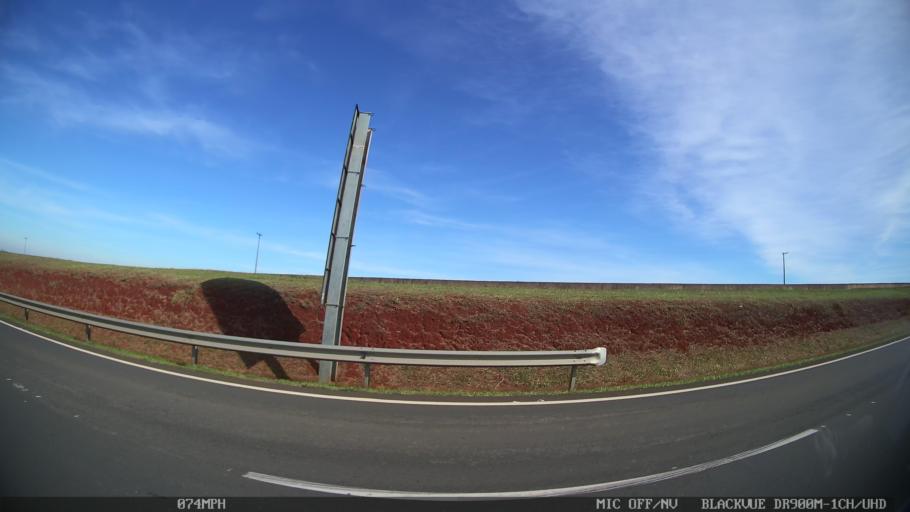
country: BR
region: Sao Paulo
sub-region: Cordeiropolis
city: Cordeiropolis
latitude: -22.4750
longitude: -47.3990
